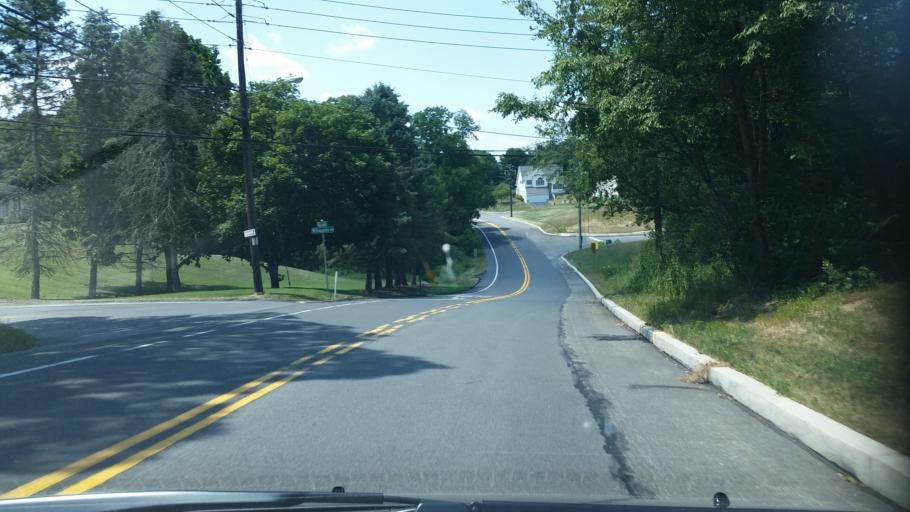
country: US
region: Pennsylvania
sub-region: Dauphin County
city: Rutherford
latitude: 40.2900
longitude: -76.7547
